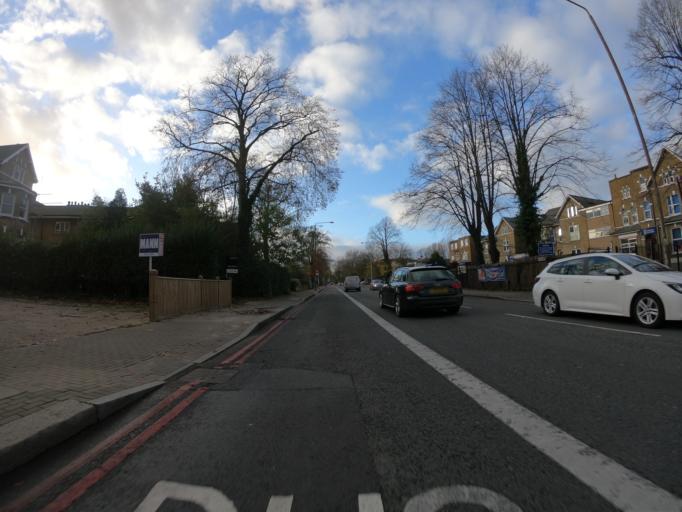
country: GB
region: England
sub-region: Greater London
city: Blackheath
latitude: 51.4544
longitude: 0.0203
